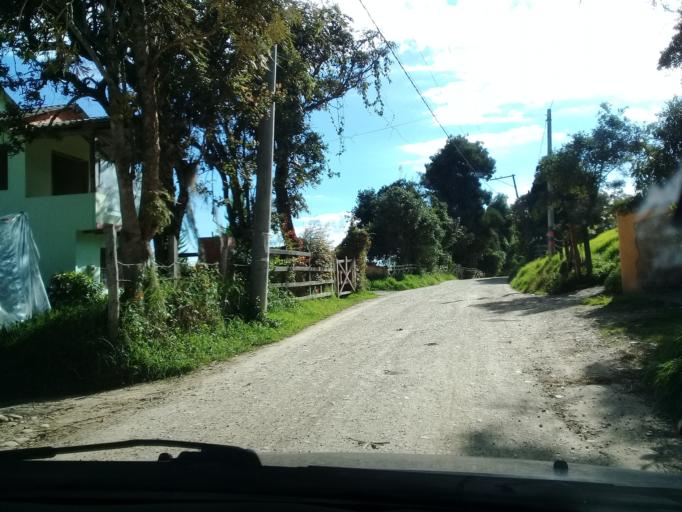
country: CO
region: Cundinamarca
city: Tabio
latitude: 4.9700
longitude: -74.0746
